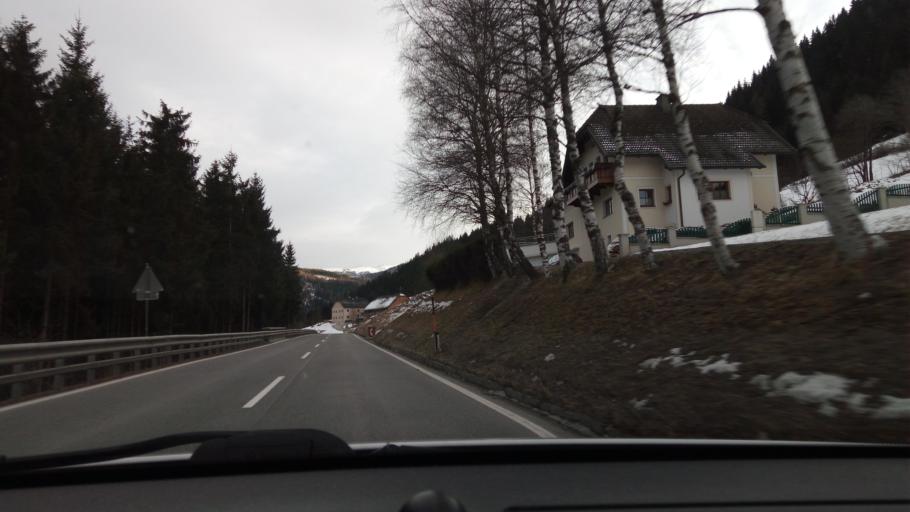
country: AT
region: Salzburg
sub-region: Politischer Bezirk Tamsweg
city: Tamsweg
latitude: 47.1058
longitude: 13.8175
